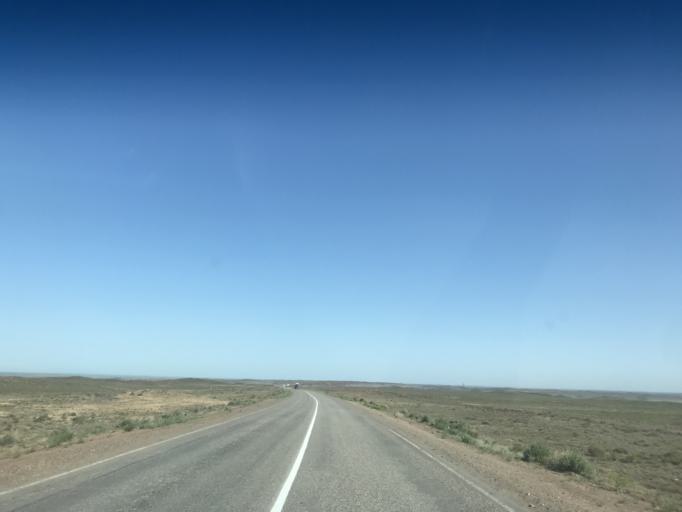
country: KZ
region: Zhambyl
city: Mynaral
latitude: 45.4706
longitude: 73.5577
